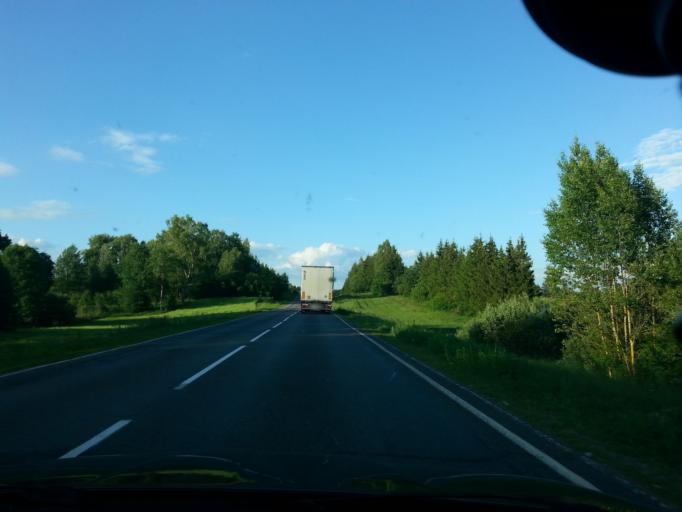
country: BY
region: Minsk
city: Svir
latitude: 54.8763
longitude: 26.3602
